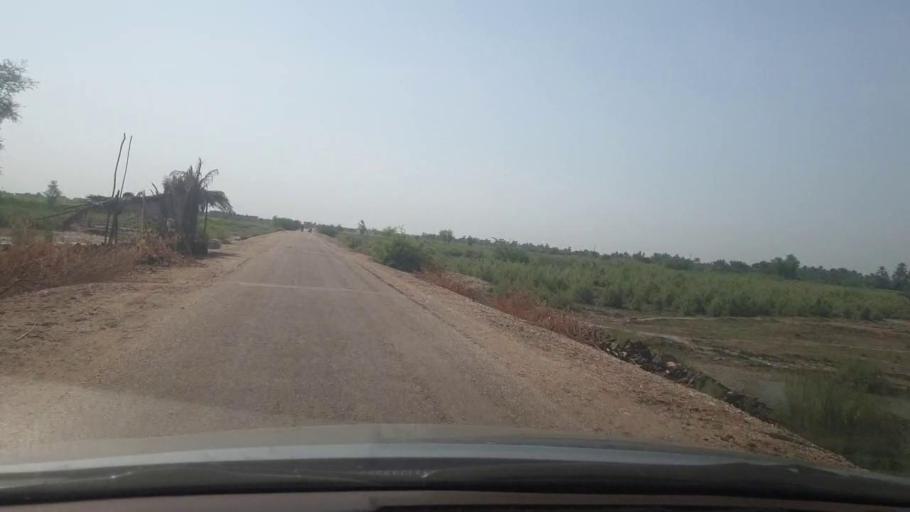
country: PK
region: Sindh
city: Ranipur
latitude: 27.2636
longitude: 68.5824
